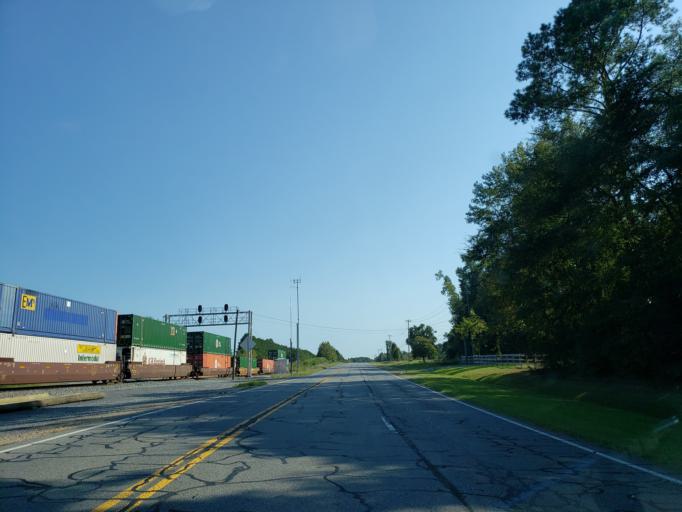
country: US
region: Georgia
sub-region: Whitfield County
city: Varnell
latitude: 34.8946
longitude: -84.9750
